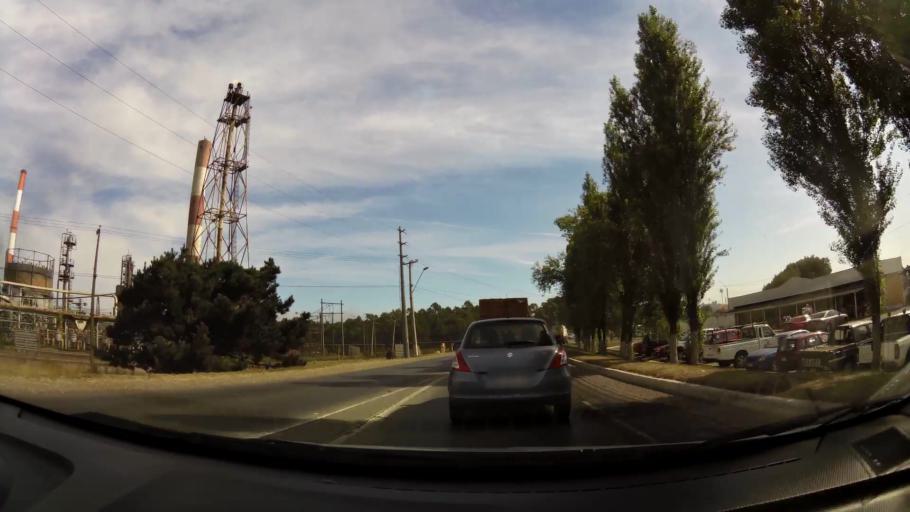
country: CL
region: Biobio
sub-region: Provincia de Concepcion
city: Talcahuano
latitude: -36.7389
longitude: -73.1209
